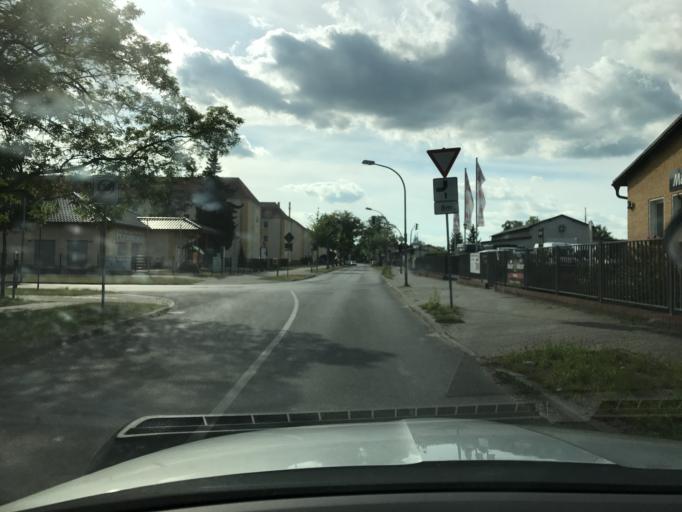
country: DE
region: Brandenburg
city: Falkensee
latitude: 52.5618
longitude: 13.0780
